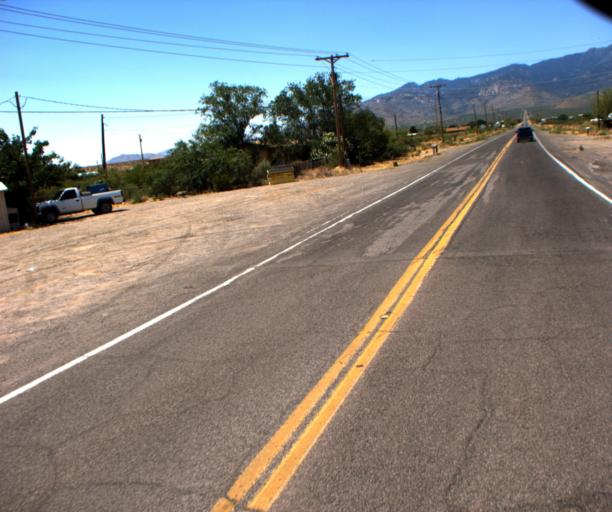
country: US
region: Arizona
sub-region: Graham County
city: Swift Trail Junction
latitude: 32.7296
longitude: -109.7146
